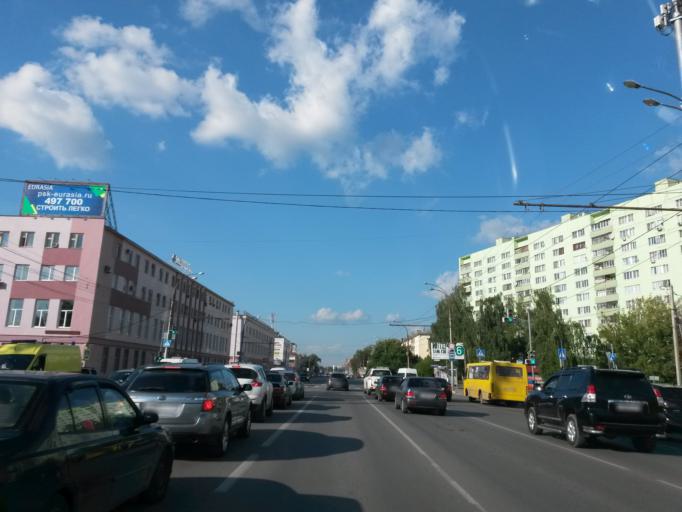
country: RU
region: Ivanovo
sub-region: Gorod Ivanovo
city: Ivanovo
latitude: 56.9754
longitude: 40.9751
